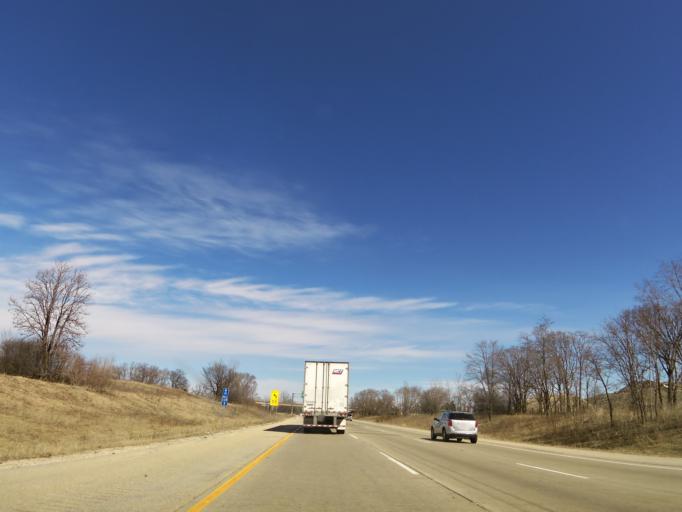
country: US
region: Wisconsin
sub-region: Dane County
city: Monona
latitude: 43.0959
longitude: -89.2850
